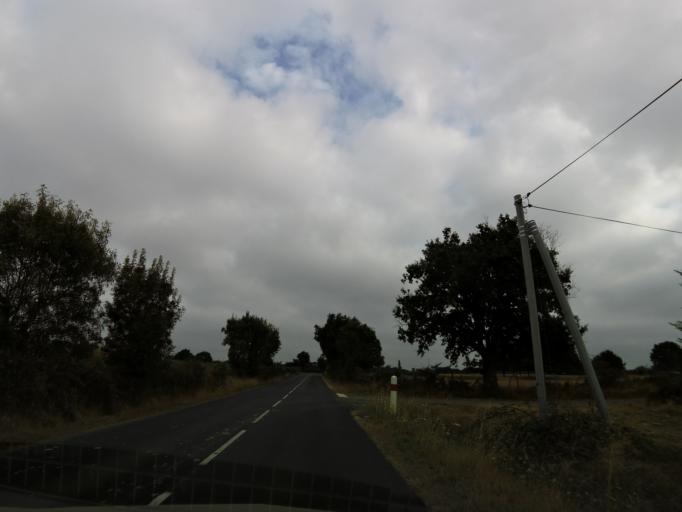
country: FR
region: Pays de la Loire
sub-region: Departement de la Vendee
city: Avrille
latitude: 46.4558
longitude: -1.4588
